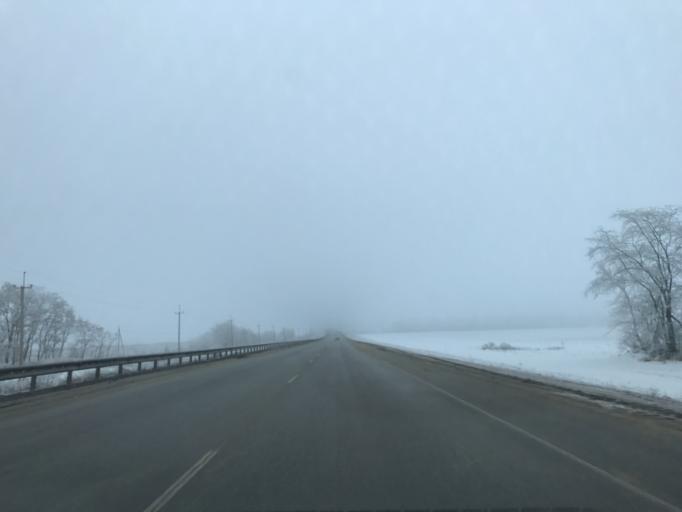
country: RU
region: Rostov
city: Grushevskaya
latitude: 47.3786
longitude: 39.8554
